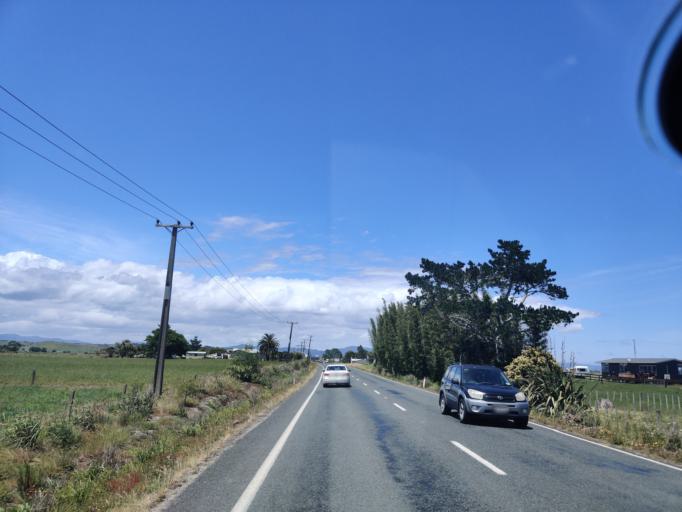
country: NZ
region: Northland
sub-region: Far North District
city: Kaitaia
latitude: -35.0331
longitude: 173.2542
